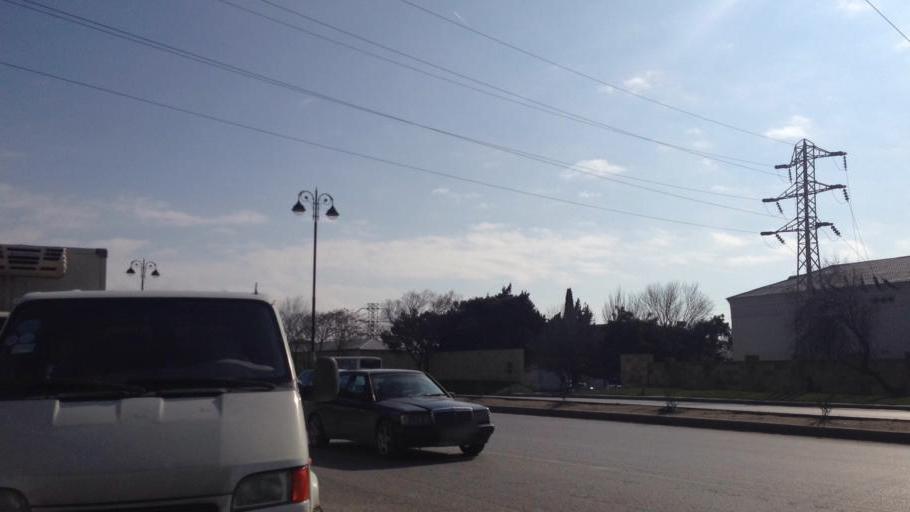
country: AZ
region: Baki
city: Baku
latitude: 40.3755
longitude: 49.9212
